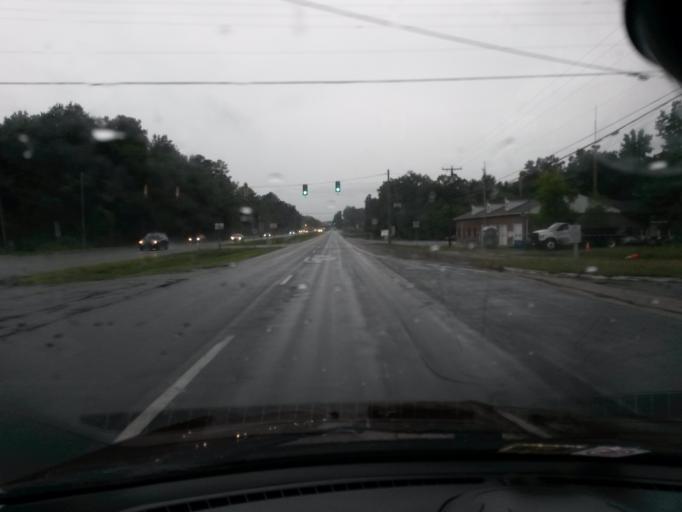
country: US
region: Virginia
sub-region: Chesterfield County
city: Enon
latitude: 37.3310
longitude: -77.3229
